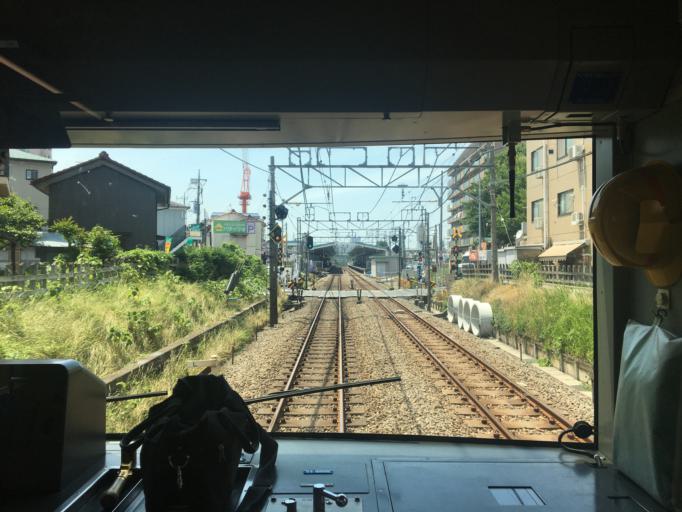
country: JP
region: Saitama
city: Tokorozawa
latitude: 35.7778
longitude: 139.4992
